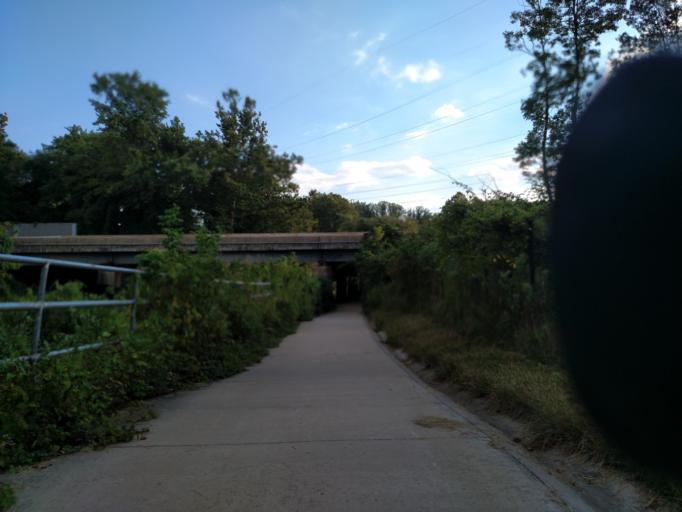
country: US
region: Virginia
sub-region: Fairfax County
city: Annandale
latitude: 38.8337
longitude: -77.2194
